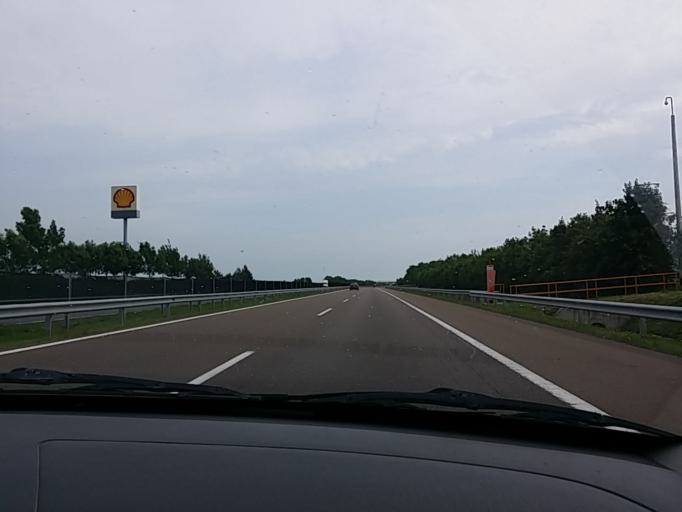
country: HU
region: Borsod-Abauj-Zemplen
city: Mezokeresztes
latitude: 47.8422
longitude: 20.7434
